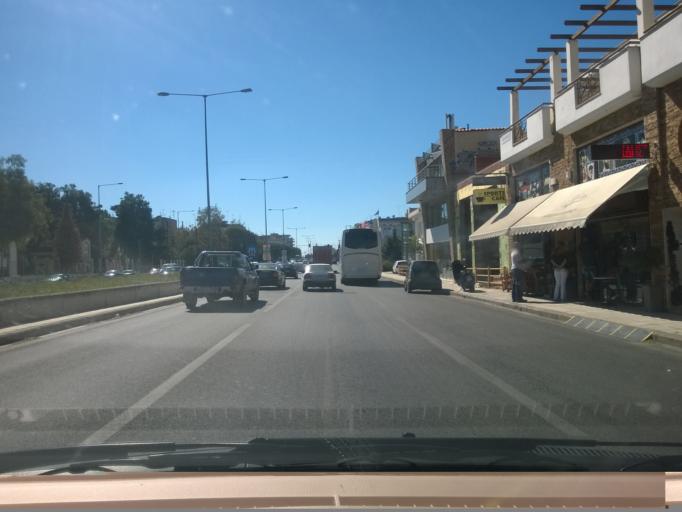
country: GR
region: Central Macedonia
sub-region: Nomos Thessalonikis
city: Stavroupoli
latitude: 40.6665
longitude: 22.9370
